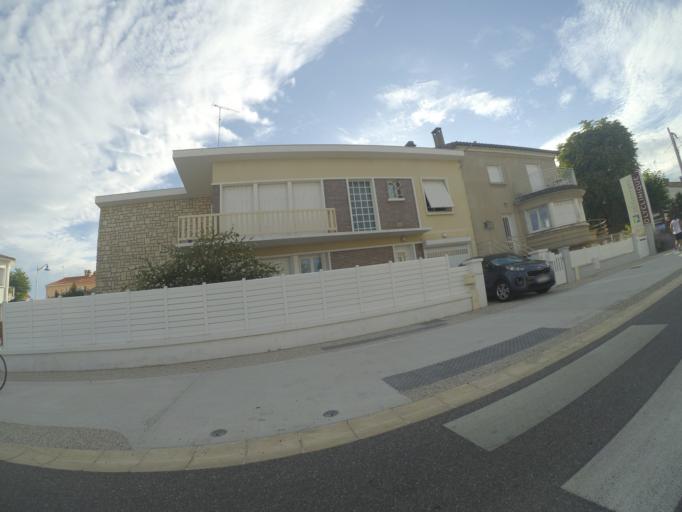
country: FR
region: Poitou-Charentes
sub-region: Departement de la Charente-Maritime
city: Saint-Georges-de-Didonne
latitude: 45.6023
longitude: -1.0024
